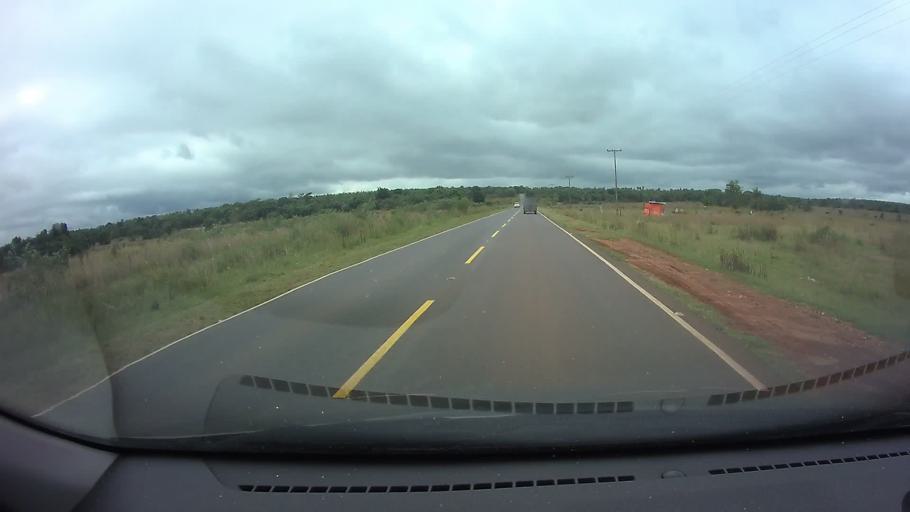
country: PY
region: Paraguari
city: Yaguaron
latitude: -25.7139
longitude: -57.3385
